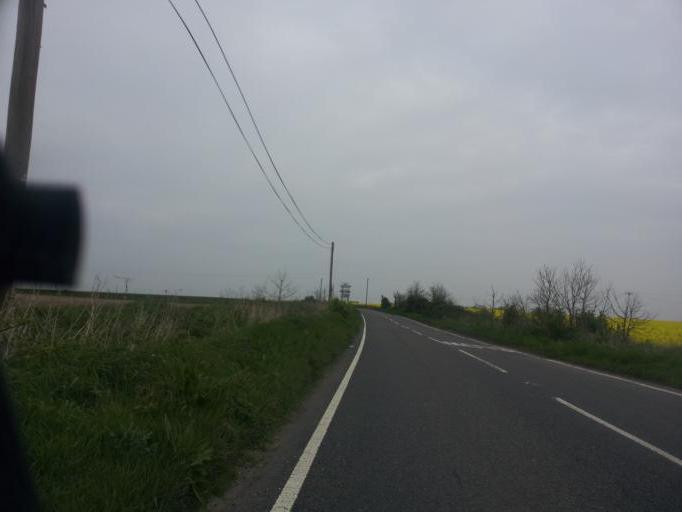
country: GB
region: England
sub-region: Medway
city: Stoke
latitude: 51.4665
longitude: 0.6223
